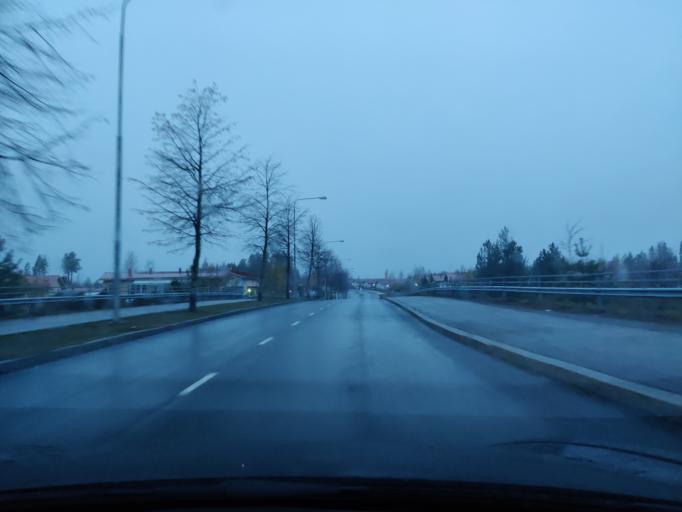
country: FI
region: Northern Savo
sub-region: Kuopio
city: Kuopio
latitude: 62.8258
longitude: 27.6910
